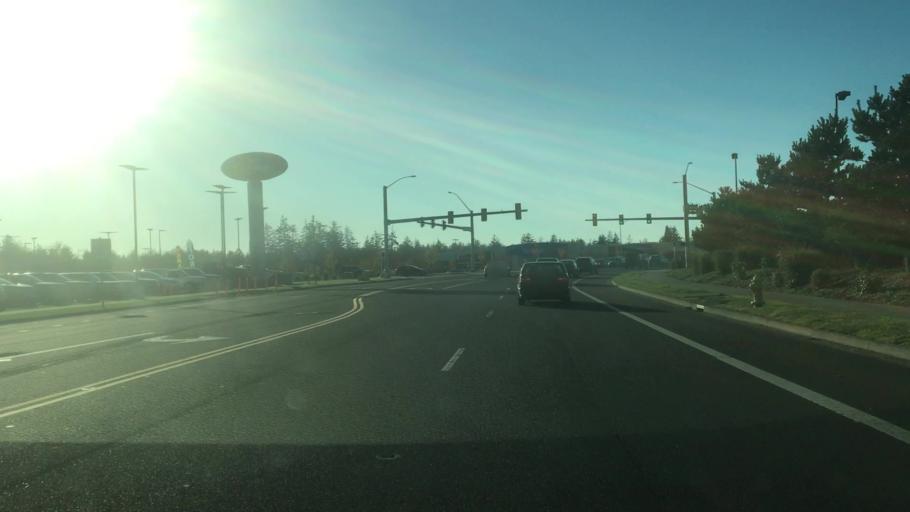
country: US
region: Oregon
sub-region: Clatsop County
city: Warrenton
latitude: 46.1452
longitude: -123.9129
